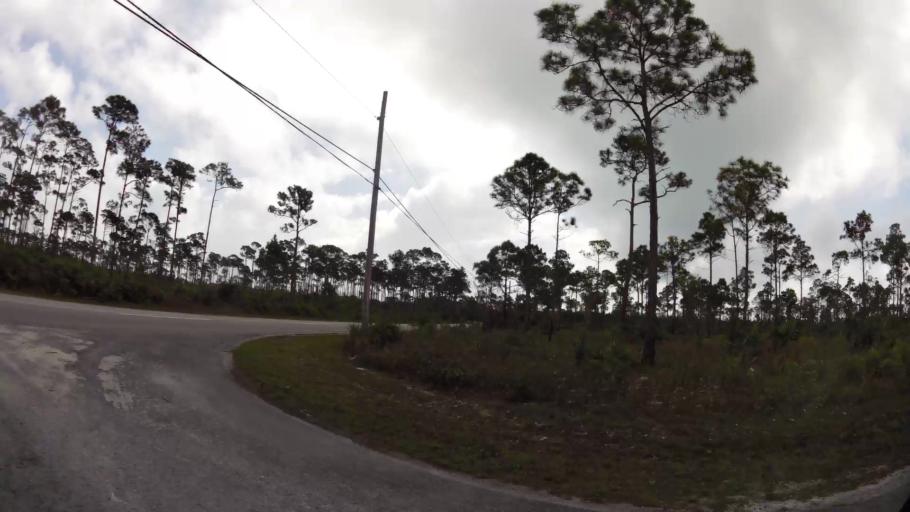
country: BS
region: Freeport
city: Lucaya
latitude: 26.5365
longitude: -78.6013
